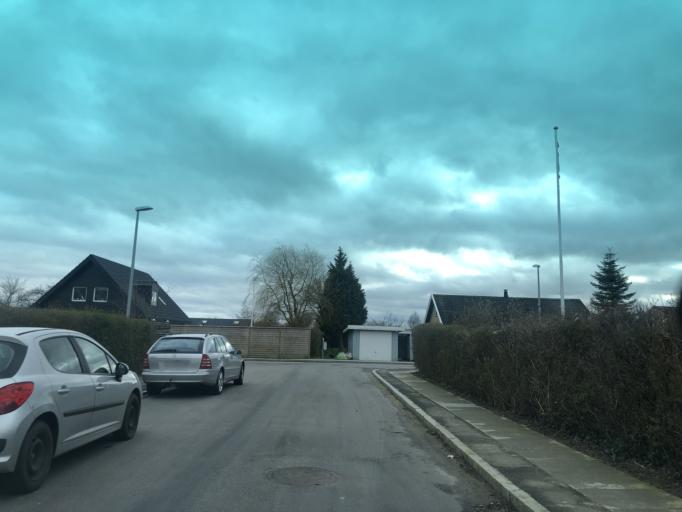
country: DK
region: Capital Region
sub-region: Tarnby Kommune
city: Tarnby
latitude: 55.6017
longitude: 12.5890
